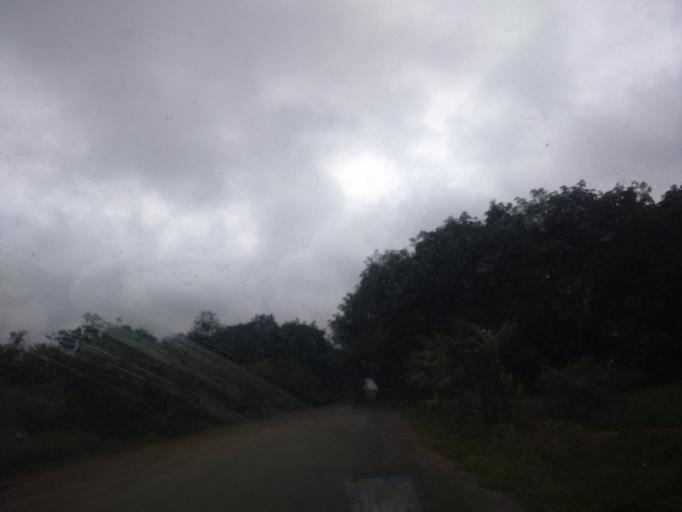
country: CI
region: Sud-Comoe
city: Bonoua
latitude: 5.2847
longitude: -3.4704
